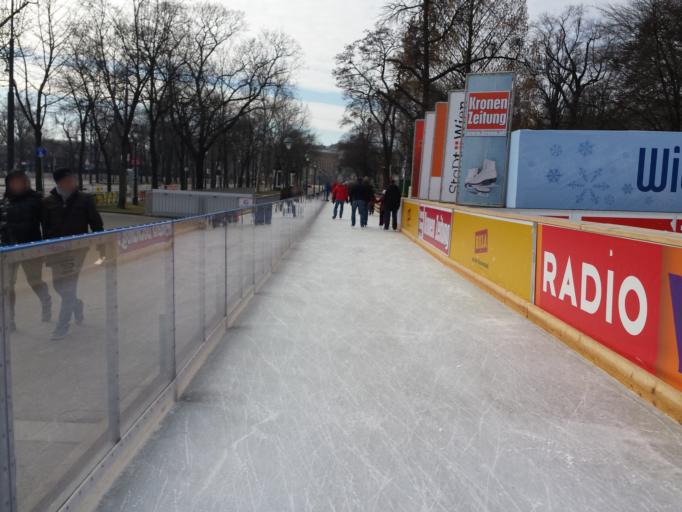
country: AT
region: Vienna
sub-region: Wien Stadt
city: Vienna
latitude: 48.2104
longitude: 16.3603
